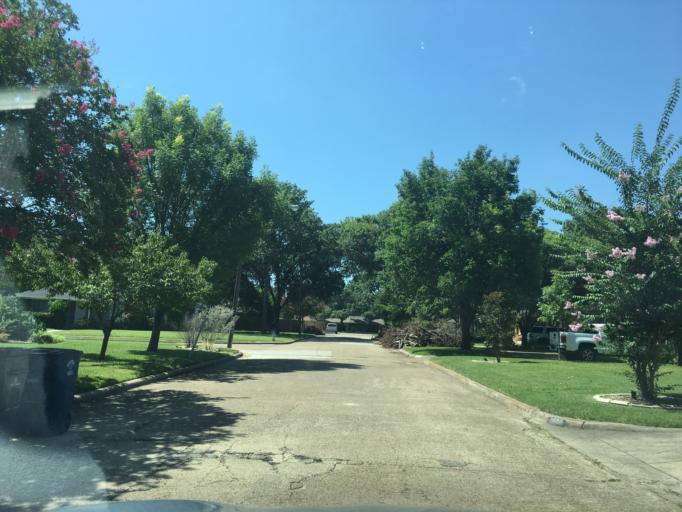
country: US
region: Texas
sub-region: Dallas County
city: Highland Park
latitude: 32.8435
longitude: -96.7462
